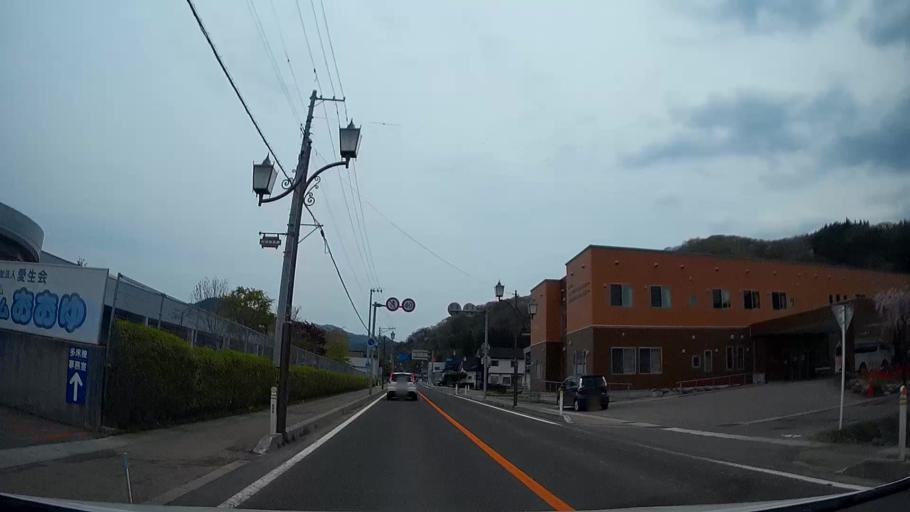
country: JP
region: Akita
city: Hanawa
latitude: 40.2960
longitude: 140.8347
